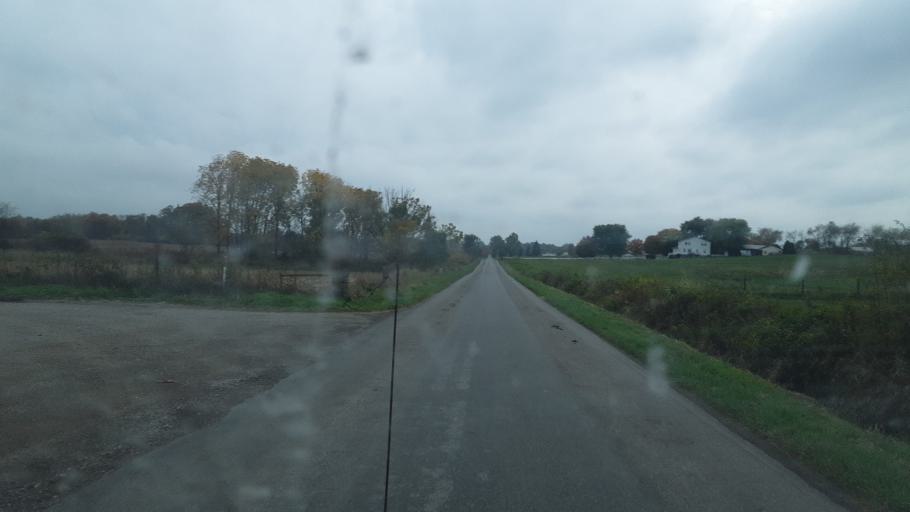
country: US
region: Ohio
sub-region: Wayne County
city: Apple Creek
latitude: 40.7070
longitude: -81.8770
